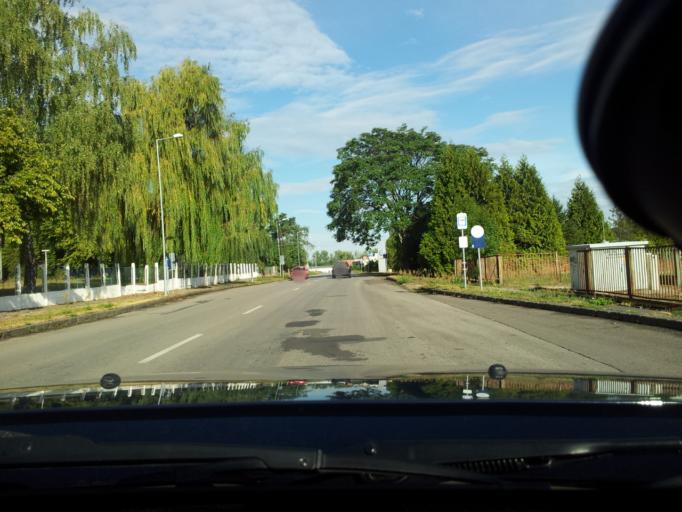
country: SK
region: Kosicky
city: Michalovce
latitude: 48.7658
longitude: 21.9038
